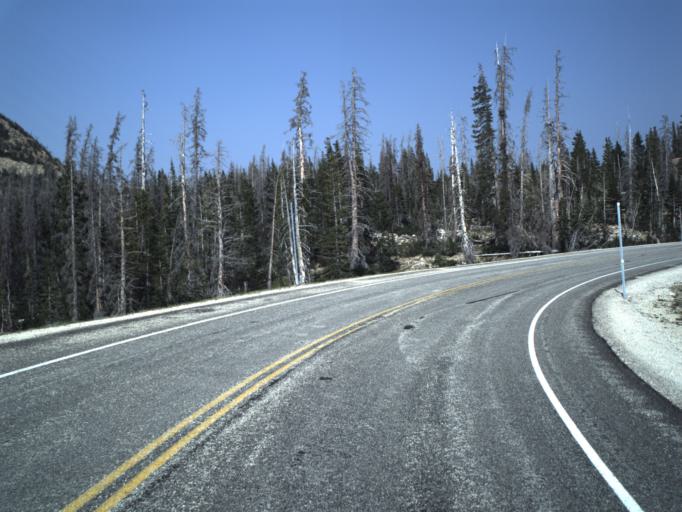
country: US
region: Utah
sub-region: Summit County
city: Kamas
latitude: 40.6877
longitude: -110.9065
